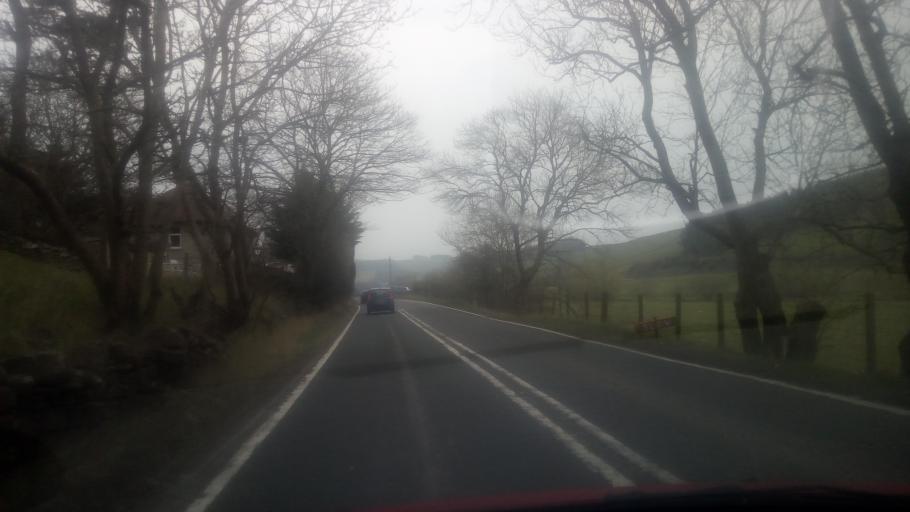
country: GB
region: Scotland
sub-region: The Scottish Borders
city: Galashiels
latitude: 55.7021
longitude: -2.8879
